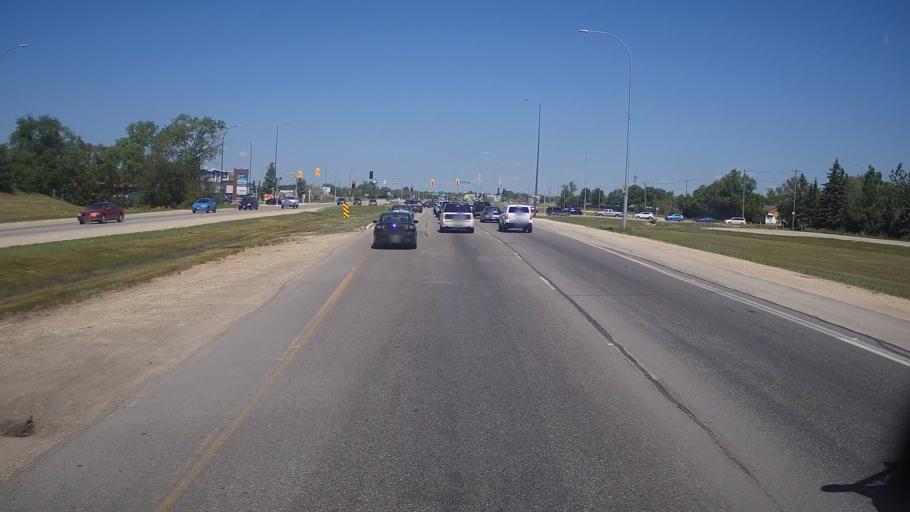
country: CA
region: Manitoba
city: Winnipeg
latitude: 49.9210
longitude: -97.0483
